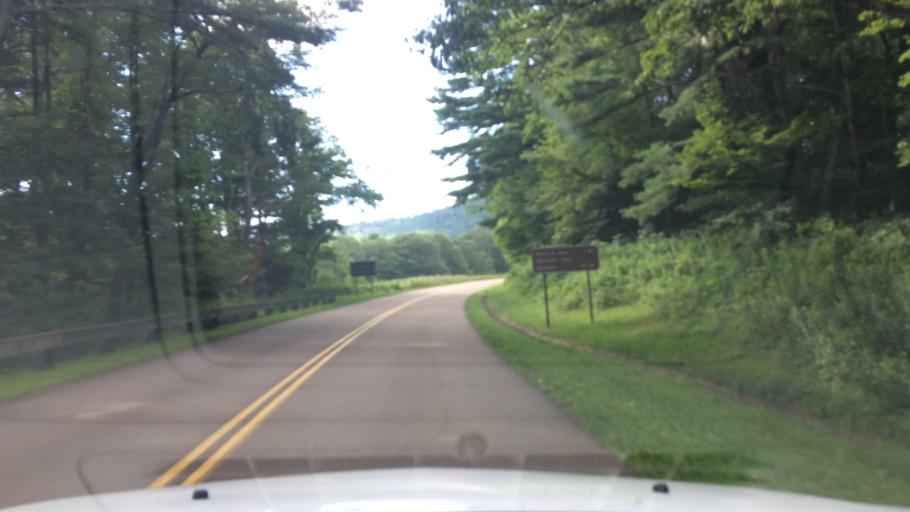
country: US
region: North Carolina
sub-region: Watauga County
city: Blowing Rock
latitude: 36.1490
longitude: -81.6645
